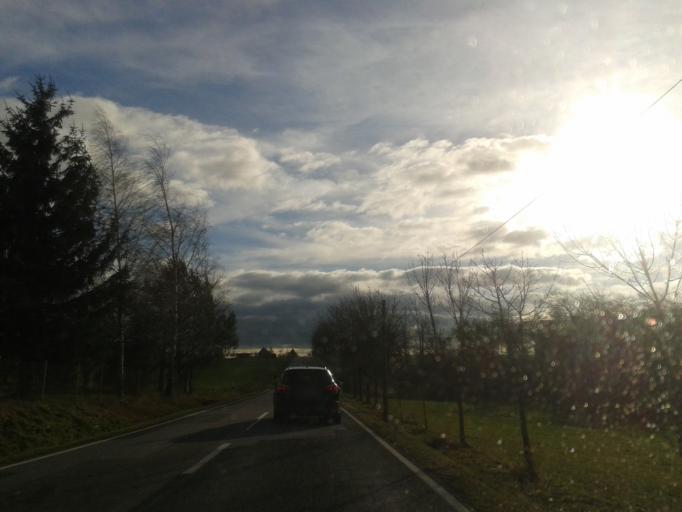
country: DE
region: Saxony
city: Weissenberg
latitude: 51.1732
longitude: 14.6515
